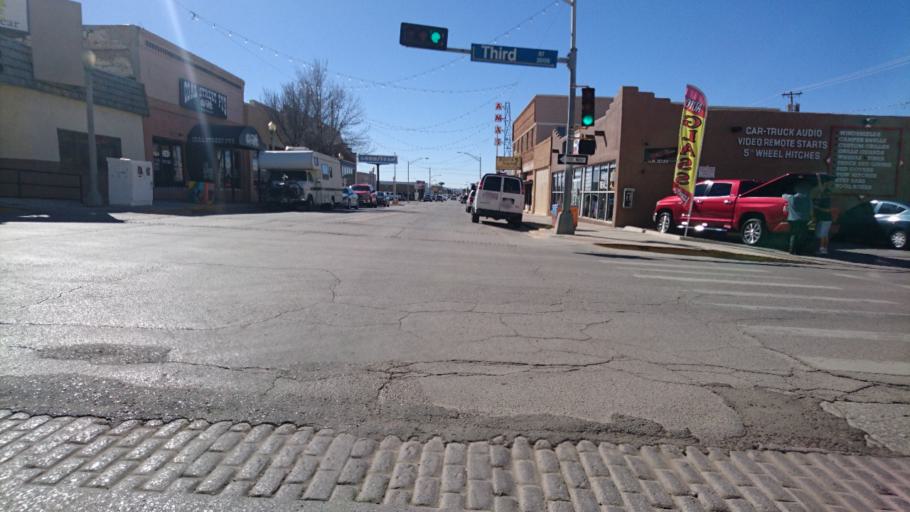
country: US
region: New Mexico
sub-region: McKinley County
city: Gallup
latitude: 35.5268
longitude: -108.7440
